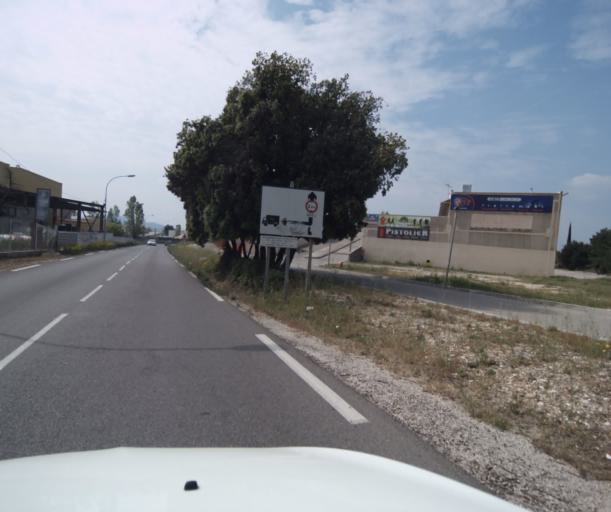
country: FR
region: Provence-Alpes-Cote d'Azur
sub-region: Departement du Var
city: La Farlede
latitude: 43.1507
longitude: 6.0378
